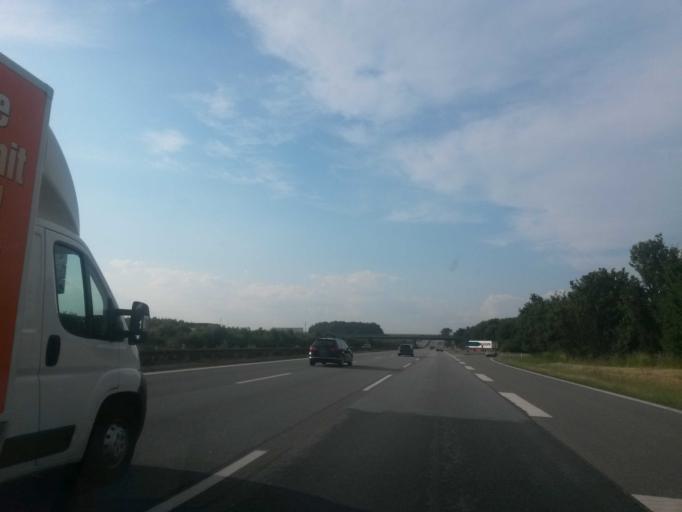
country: DE
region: Bavaria
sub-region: Upper Palatinate
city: Freystadt
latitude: 49.1595
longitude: 11.2645
